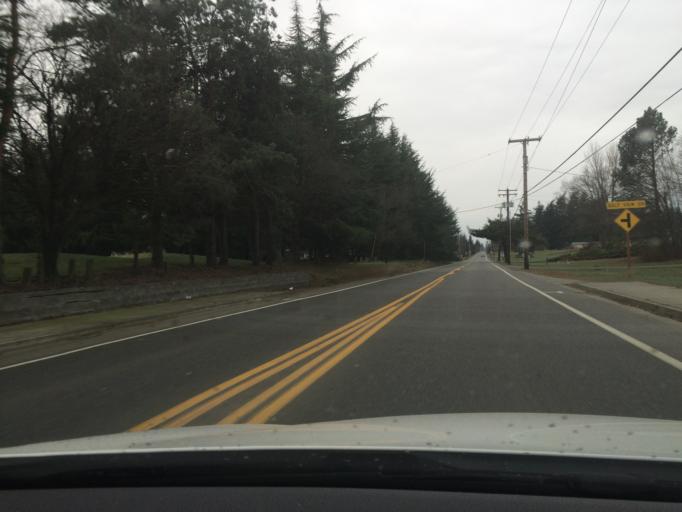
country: US
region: Washington
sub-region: Whatcom County
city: Lynden
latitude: 48.8918
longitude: -122.4448
